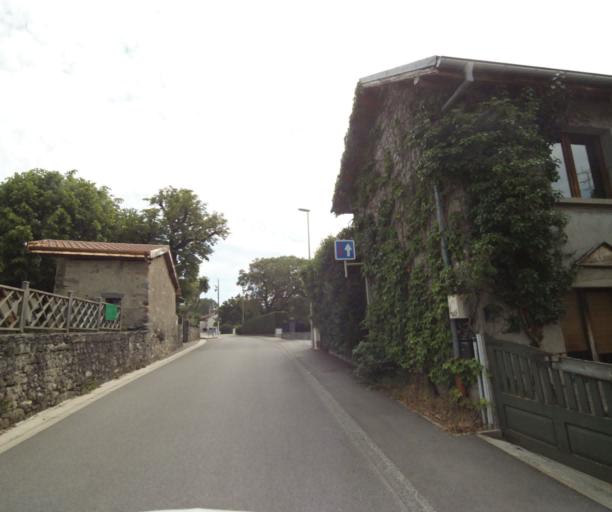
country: FR
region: Rhone-Alpes
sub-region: Departement de la Haute-Savoie
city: Margencel
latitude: 46.3381
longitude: 6.4191
